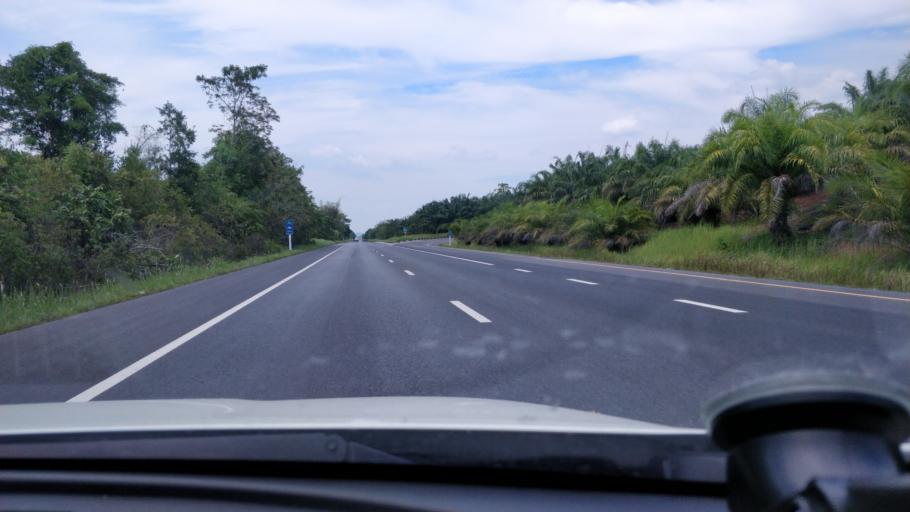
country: TH
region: Krabi
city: Plai Phraya
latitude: 8.4561
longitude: 98.8586
